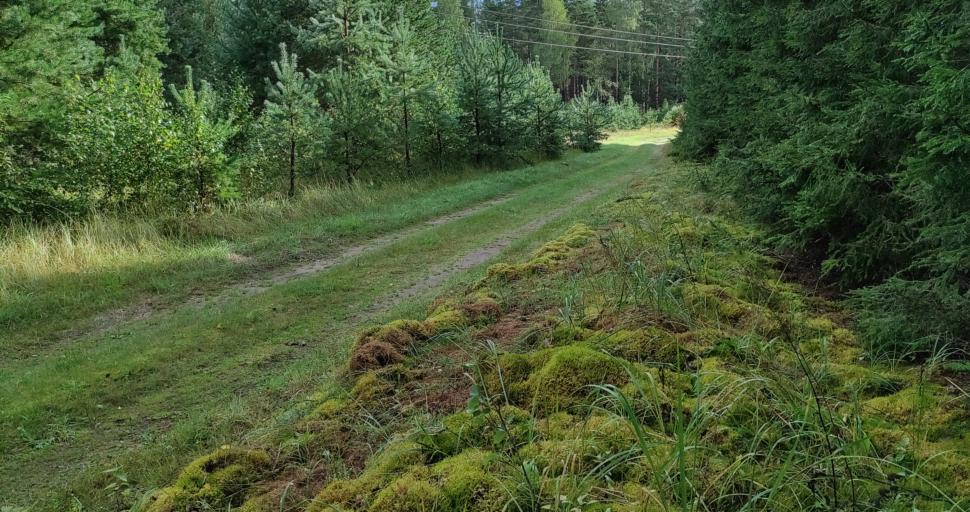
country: LV
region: Pavilostas
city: Pavilosta
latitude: 56.7741
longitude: 21.2743
